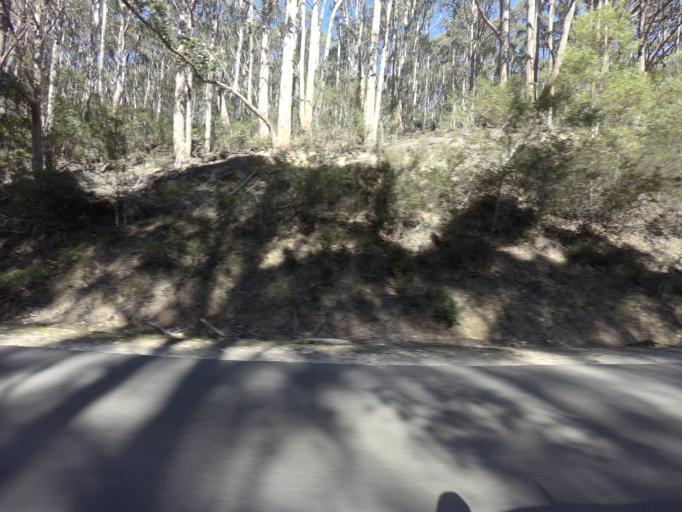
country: AU
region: Tasmania
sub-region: Derwent Valley
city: New Norfolk
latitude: -42.7308
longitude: 146.6693
